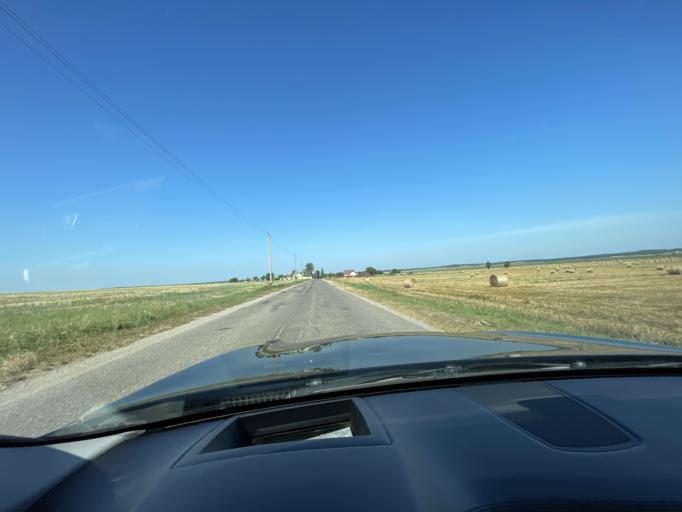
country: BY
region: Grodnenskaya
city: Hrodna
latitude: 53.7104
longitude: 23.9796
